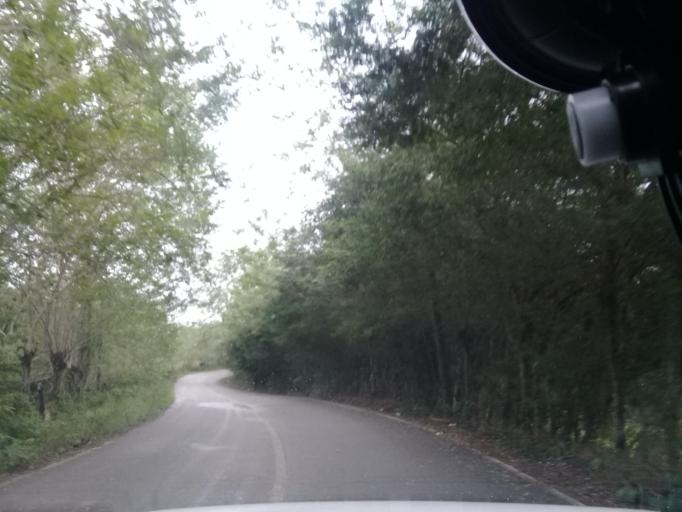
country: MX
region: Veracruz
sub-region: Chalma
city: San Pedro Coyutla
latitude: 21.2094
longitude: -98.4126
